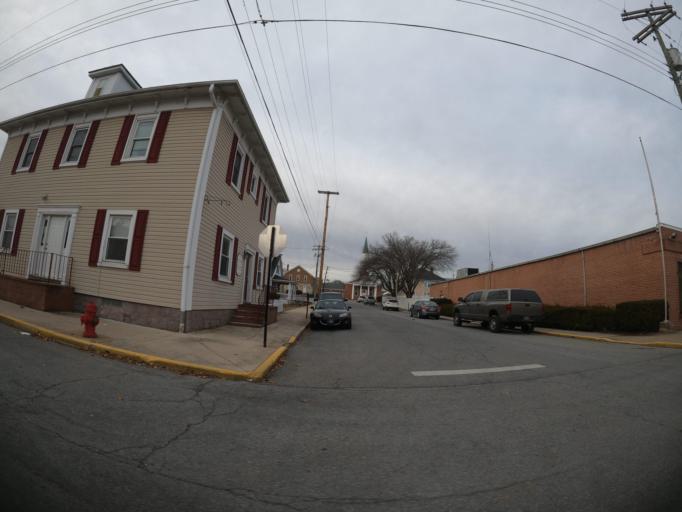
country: US
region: West Virginia
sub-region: Jefferson County
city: Charles Town
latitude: 39.2895
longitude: -77.8618
